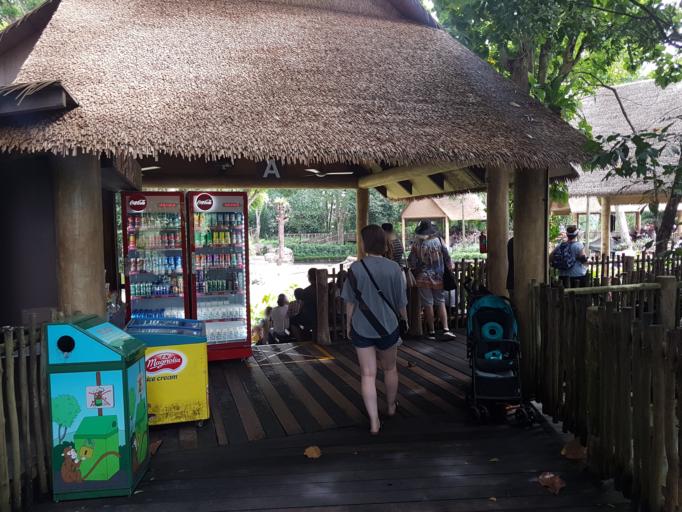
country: MY
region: Johor
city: Johor Bahru
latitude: 1.4050
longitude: 103.7960
